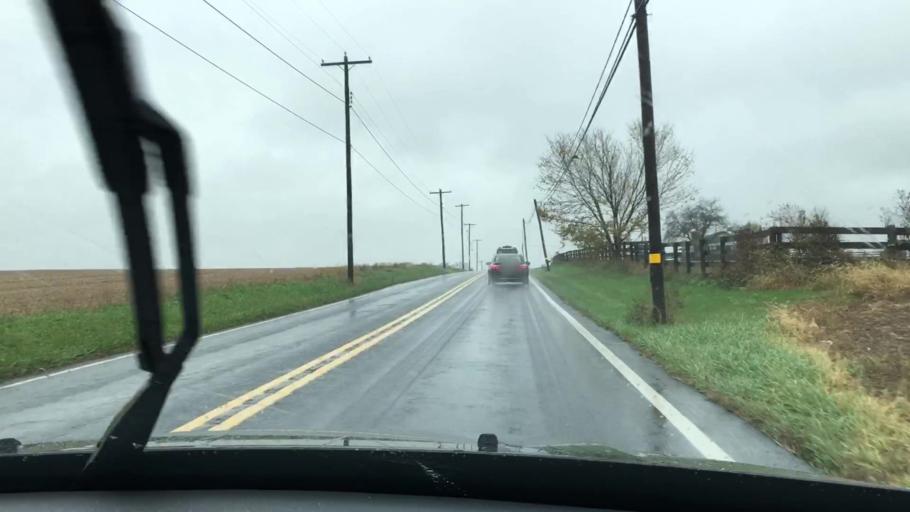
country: US
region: Maryland
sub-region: Frederick County
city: Adamstown
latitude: 39.2689
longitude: -77.4653
